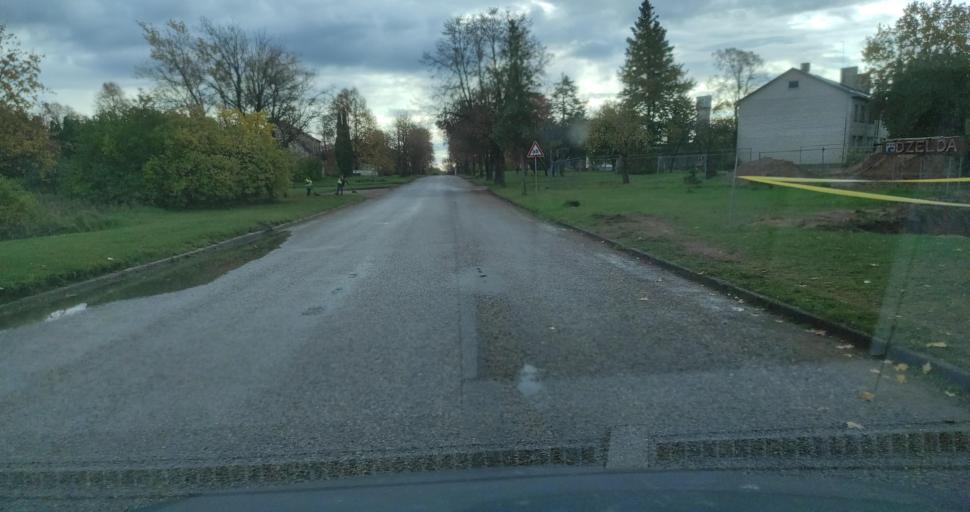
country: LV
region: Vainode
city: Vainode
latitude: 56.5711
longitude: 21.8969
